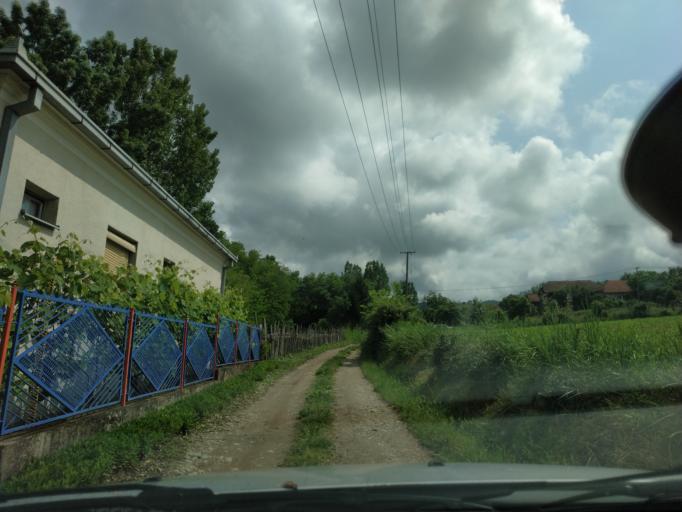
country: RS
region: Central Serbia
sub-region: Nisavski Okrug
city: Aleksinac
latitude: 43.4254
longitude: 21.5857
